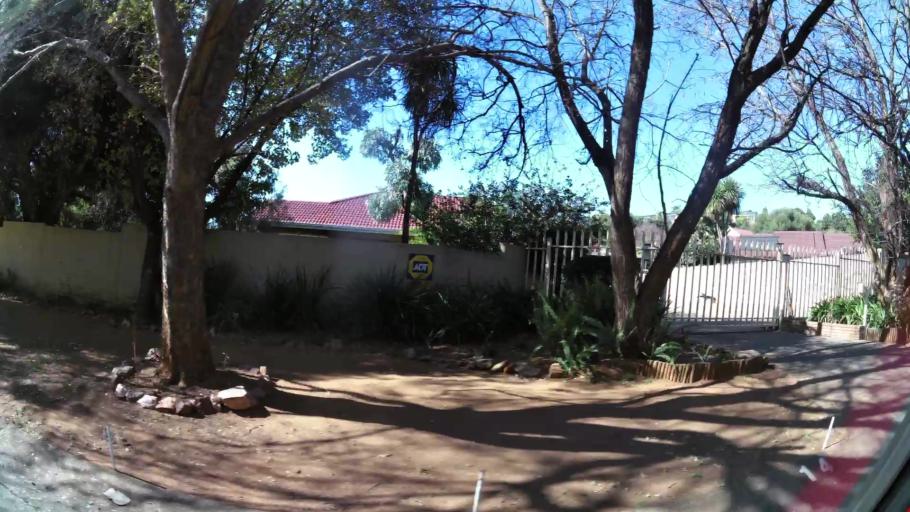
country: ZA
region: Gauteng
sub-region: City of Johannesburg Metropolitan Municipality
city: Roodepoort
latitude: -26.1163
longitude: 27.8585
